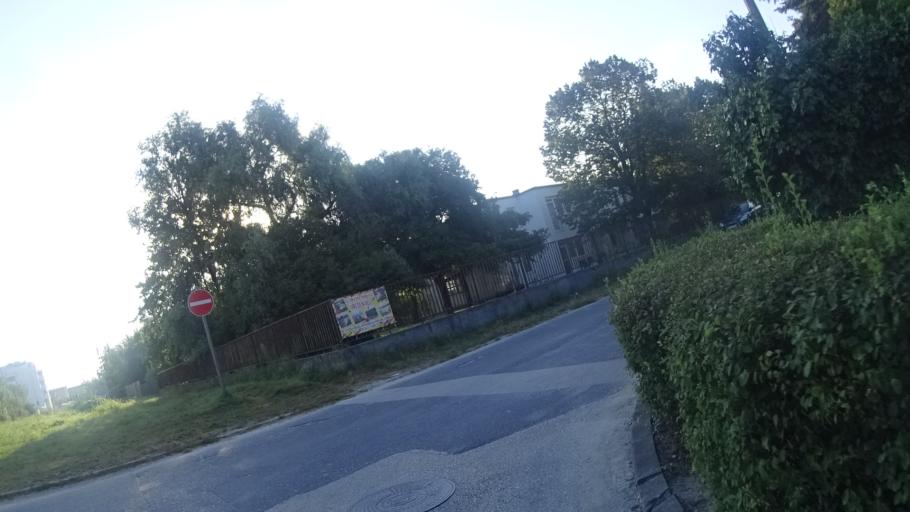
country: HU
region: Somogy
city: Siofok
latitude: 46.9248
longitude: 18.0950
